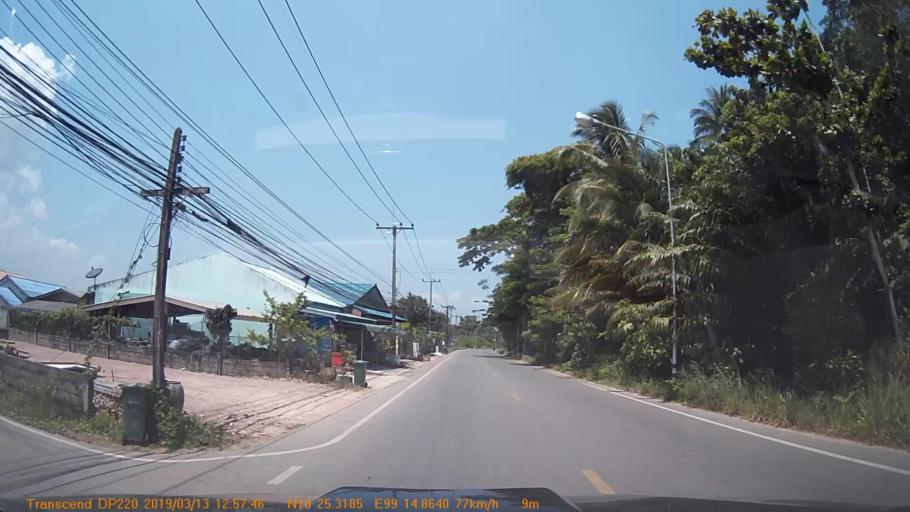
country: TH
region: Chumphon
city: Chumphon
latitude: 10.4224
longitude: 99.2477
